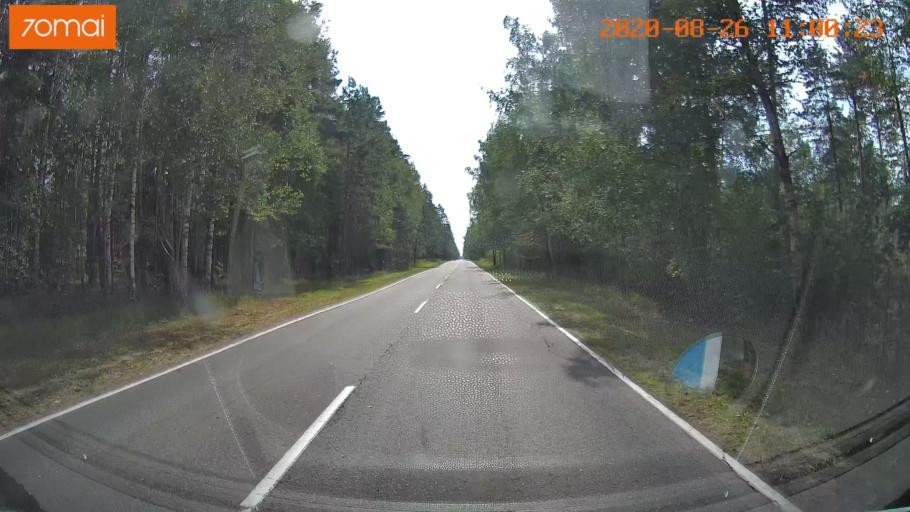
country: RU
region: Rjazan
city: Izhevskoye
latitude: 54.5757
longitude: 41.2124
